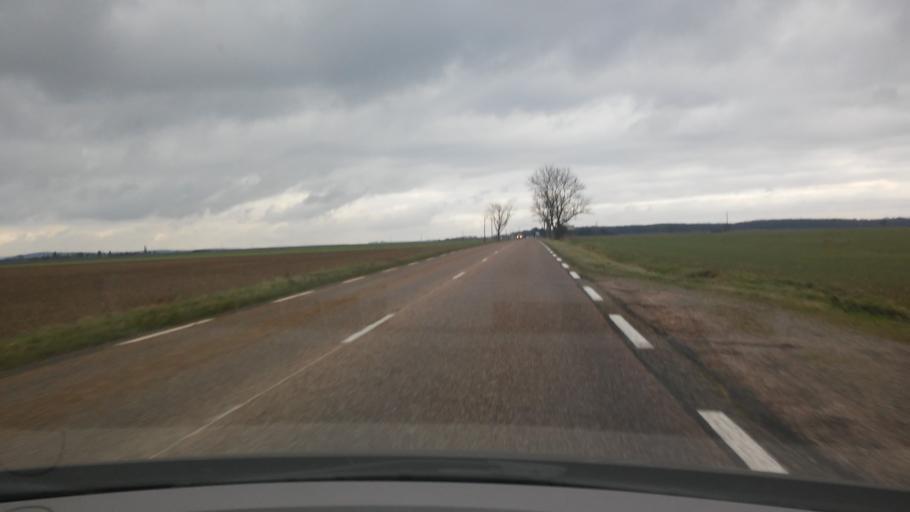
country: FR
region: Lorraine
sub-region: Departement de la Moselle
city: Retonfey
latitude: 49.1182
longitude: 6.3320
